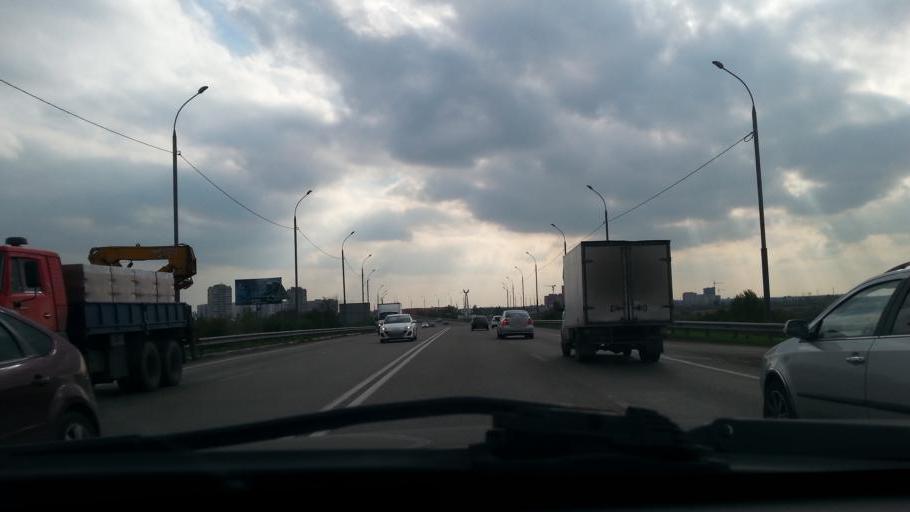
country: RU
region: Rostov
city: Bataysk
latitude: 47.1654
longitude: 39.7429
